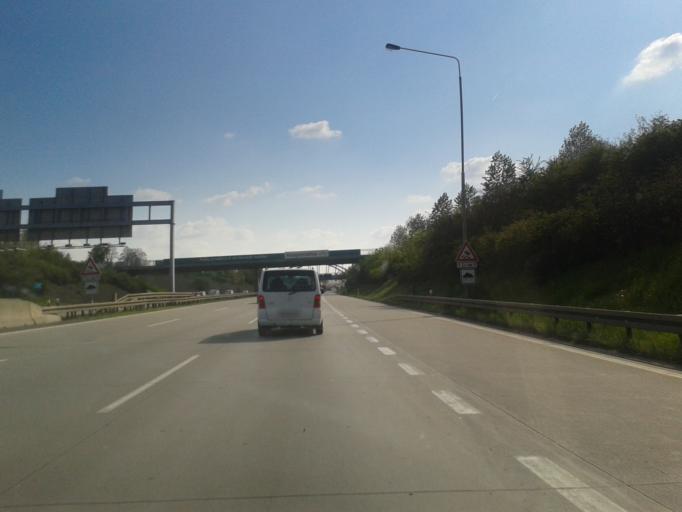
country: CZ
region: Central Bohemia
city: Hostivice
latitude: 50.0720
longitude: 14.2868
